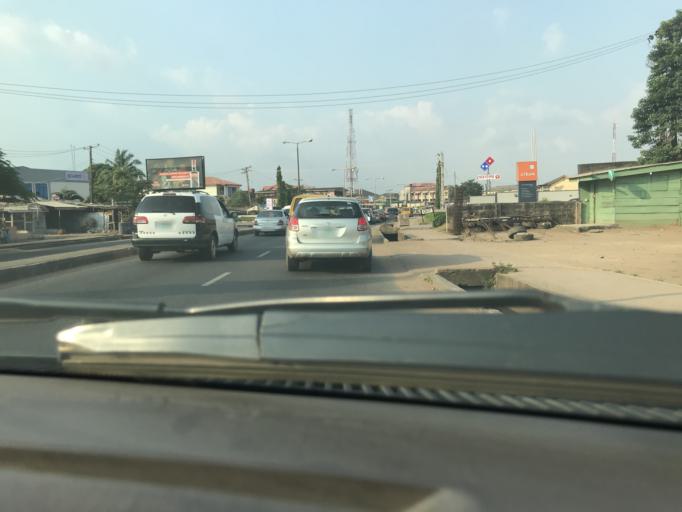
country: NG
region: Lagos
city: Ikotun
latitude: 6.5819
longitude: 3.2835
